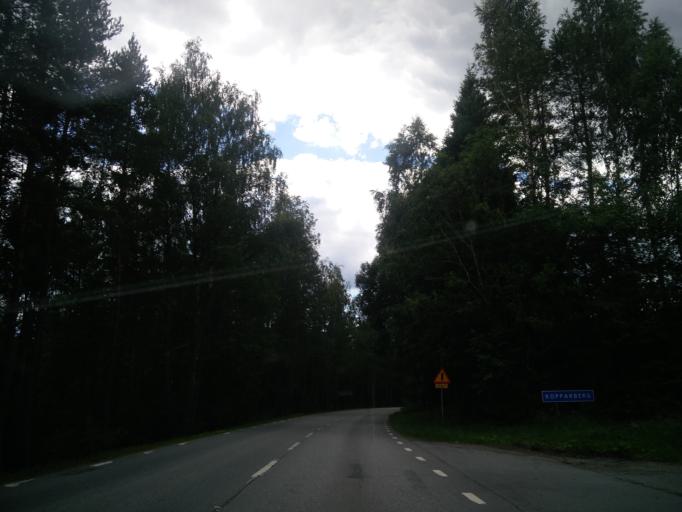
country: SE
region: OErebro
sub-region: Ljusnarsbergs Kommun
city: Kopparberg
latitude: 59.8841
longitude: 15.0107
